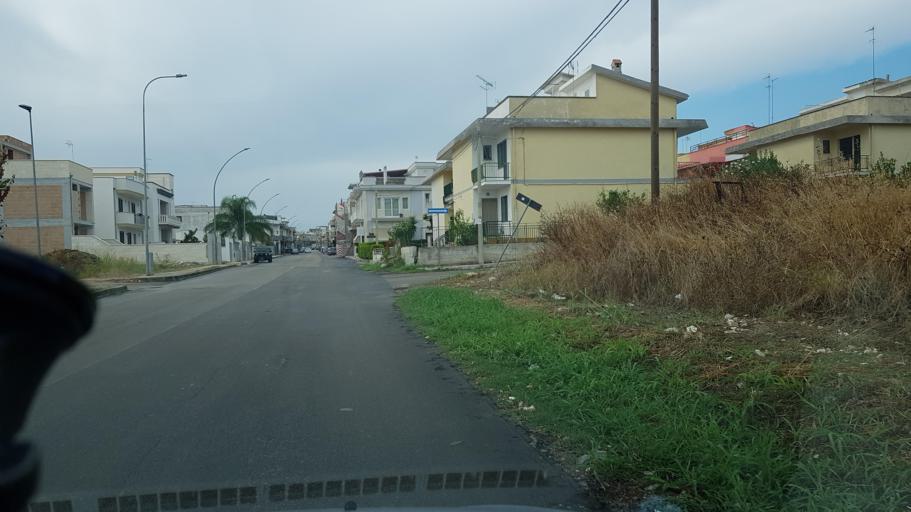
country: IT
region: Apulia
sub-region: Provincia di Brindisi
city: Oria
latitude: 40.4929
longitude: 17.6544
